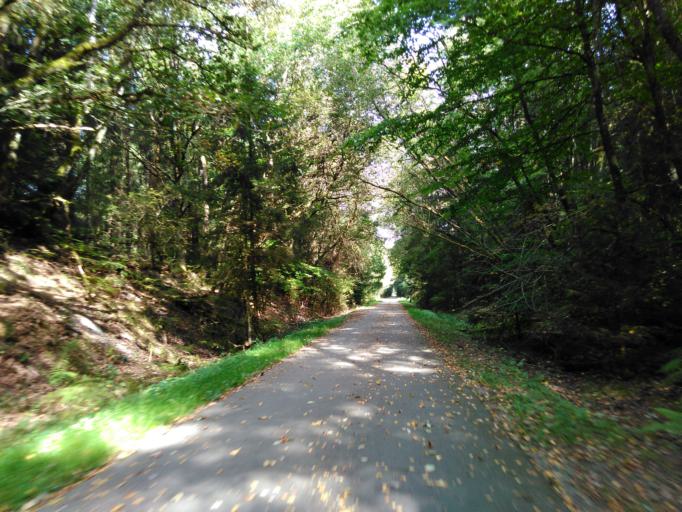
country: BE
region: Wallonia
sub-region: Province du Luxembourg
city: Gouvy
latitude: 50.1267
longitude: 5.9086
